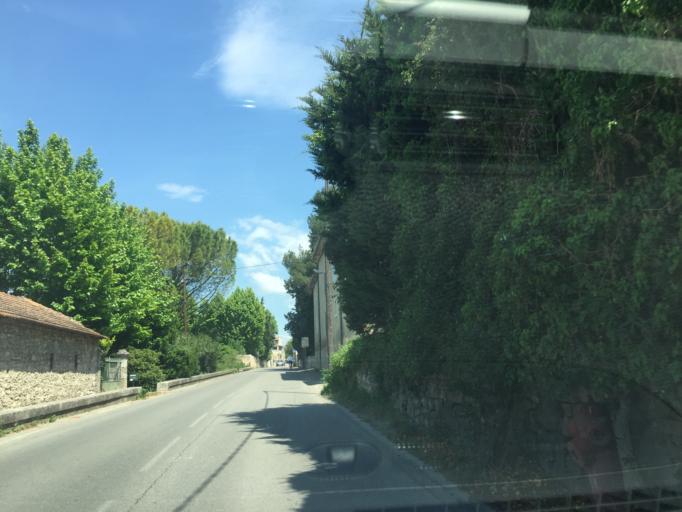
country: FR
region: Provence-Alpes-Cote d'Azur
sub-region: Departement du Vaucluse
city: Pernes-les-Fontaines
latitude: 43.9950
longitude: 5.0558
